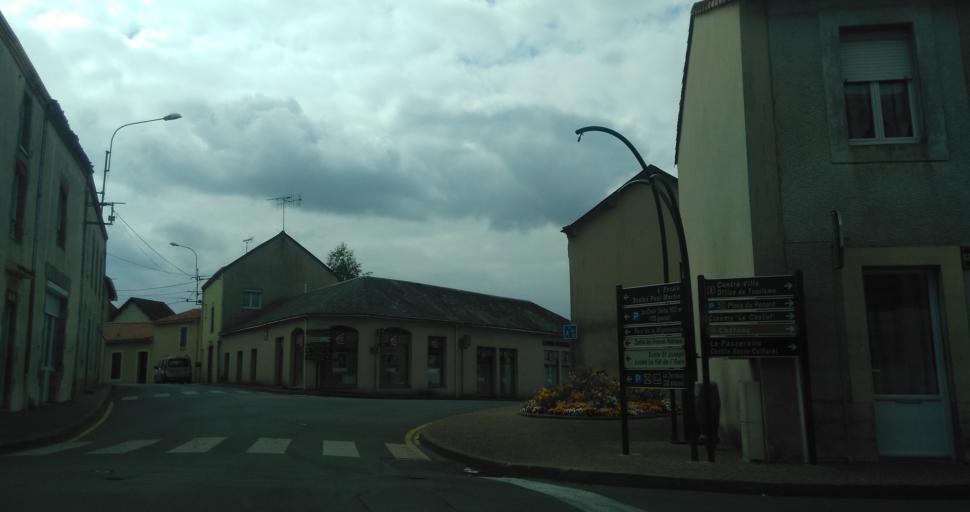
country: FR
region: Poitou-Charentes
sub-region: Departement des Deux-Sevres
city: Saint-Pierre-des-Echaubrognes
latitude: 46.9231
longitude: -0.7484
